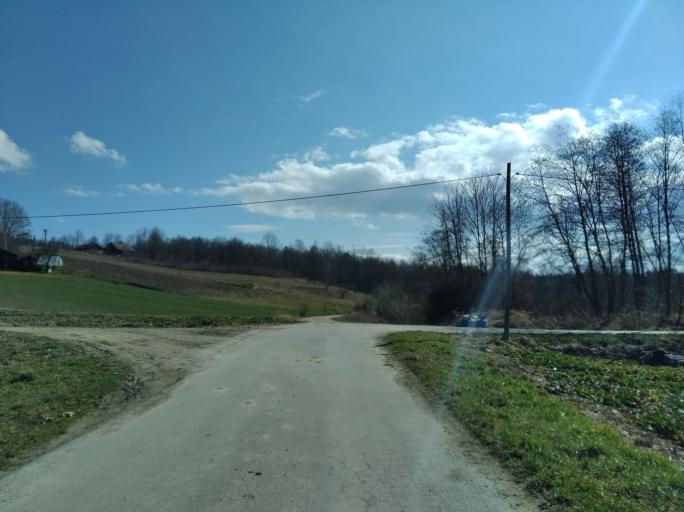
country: PL
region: Subcarpathian Voivodeship
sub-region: Powiat strzyzowski
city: Wysoka Strzyzowska
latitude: 49.8025
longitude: 21.7531
